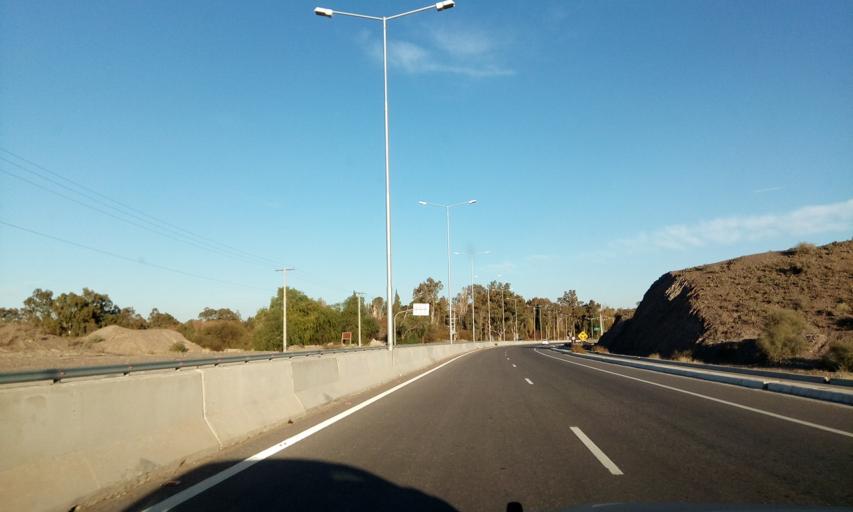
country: AR
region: San Juan
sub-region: Departamento de Rivadavia
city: Rivadavia
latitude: -31.5027
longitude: -68.6468
